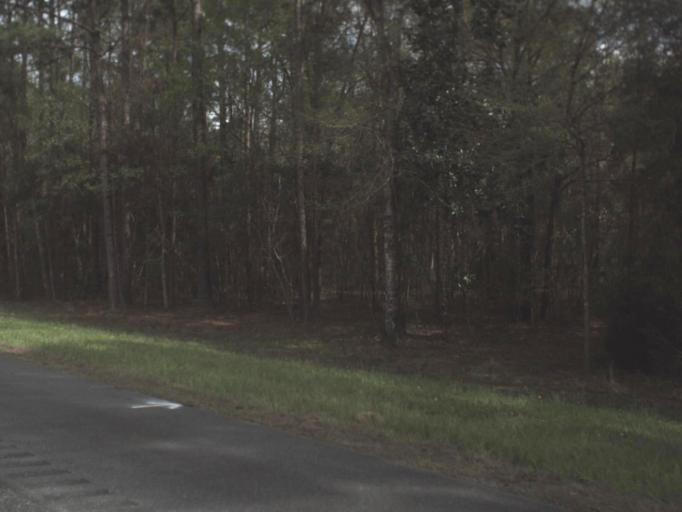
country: US
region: Florida
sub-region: Walton County
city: DeFuniak Springs
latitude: 30.6906
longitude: -86.0489
